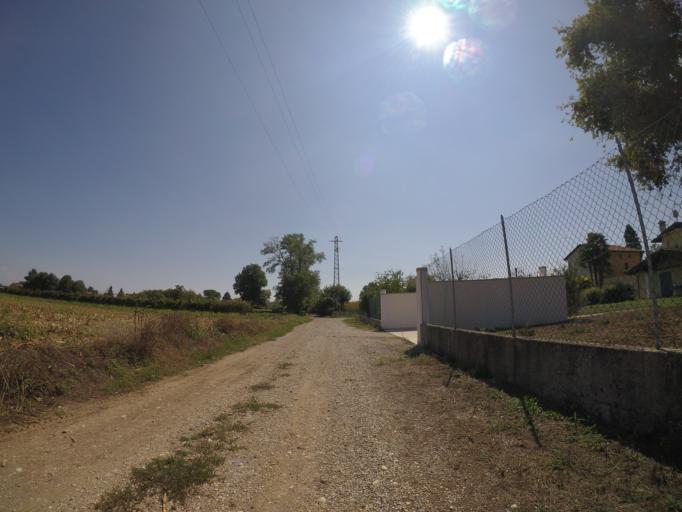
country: IT
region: Friuli Venezia Giulia
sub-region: Provincia di Udine
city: Talmassons
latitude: 45.9389
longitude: 13.0925
